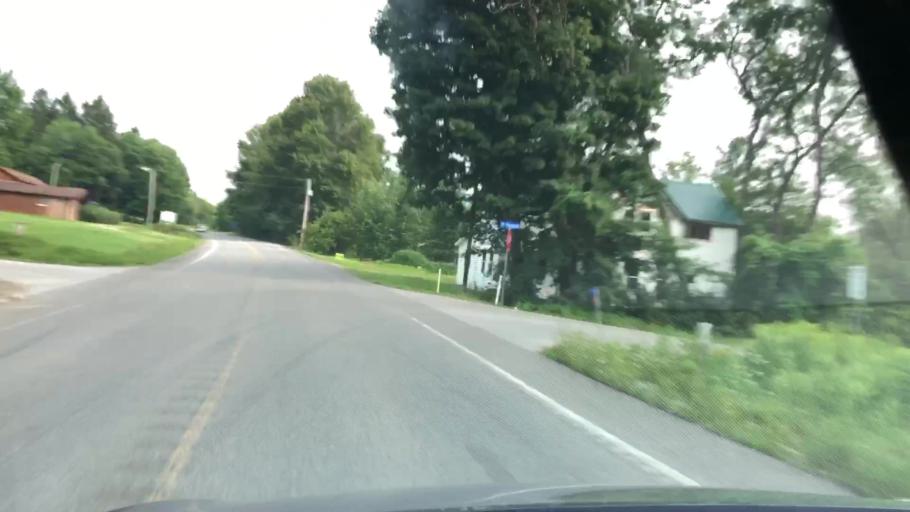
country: US
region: Pennsylvania
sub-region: Erie County
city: Union City
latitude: 41.8341
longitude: -79.8182
